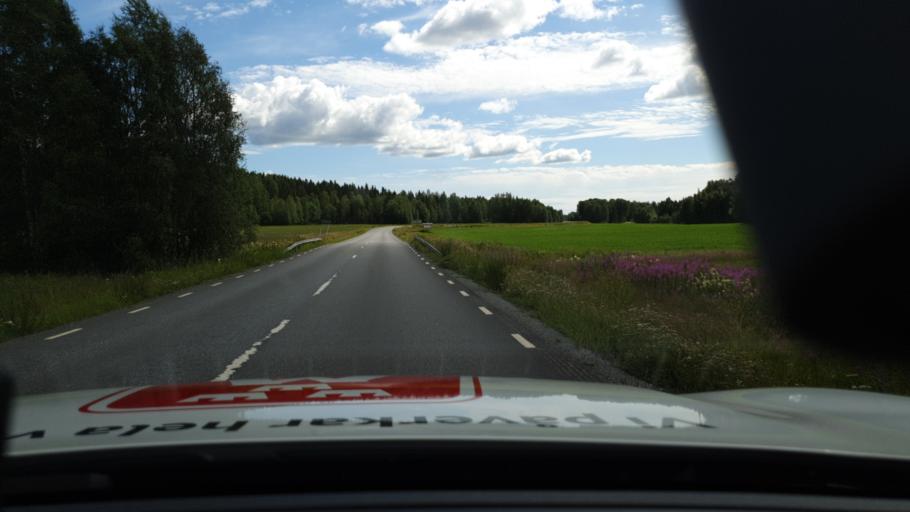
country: SE
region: Norrbotten
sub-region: Lulea Kommun
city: Sodra Sunderbyn
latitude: 65.8229
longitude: 21.9899
